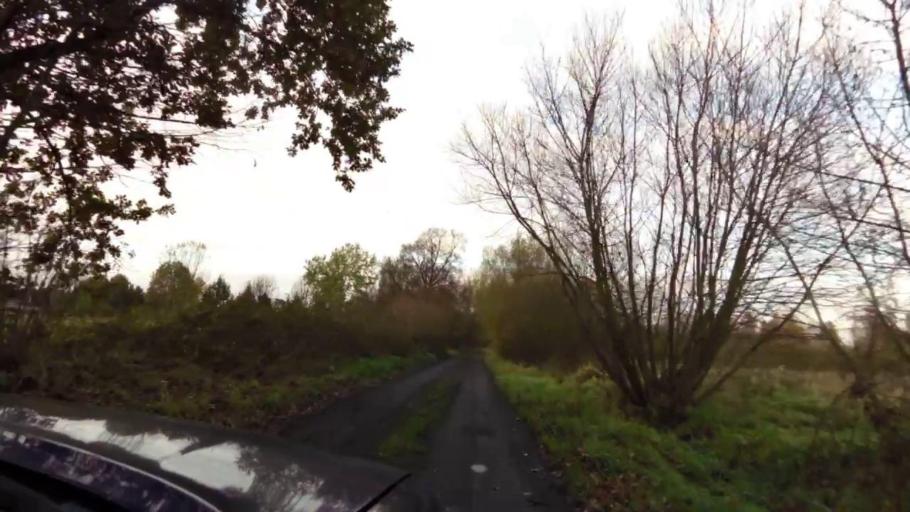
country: PL
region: West Pomeranian Voivodeship
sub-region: Powiat goleniowski
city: Goleniow
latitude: 53.5930
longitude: 14.7444
